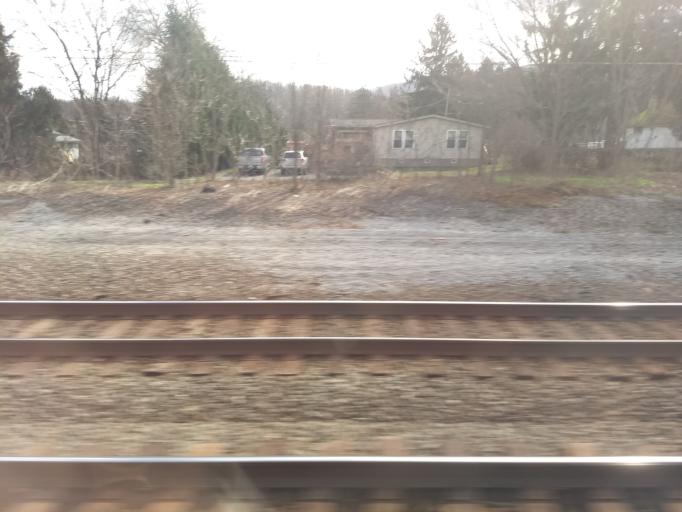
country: US
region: Pennsylvania
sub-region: Blair County
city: Bellwood
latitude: 40.6179
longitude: -78.3219
